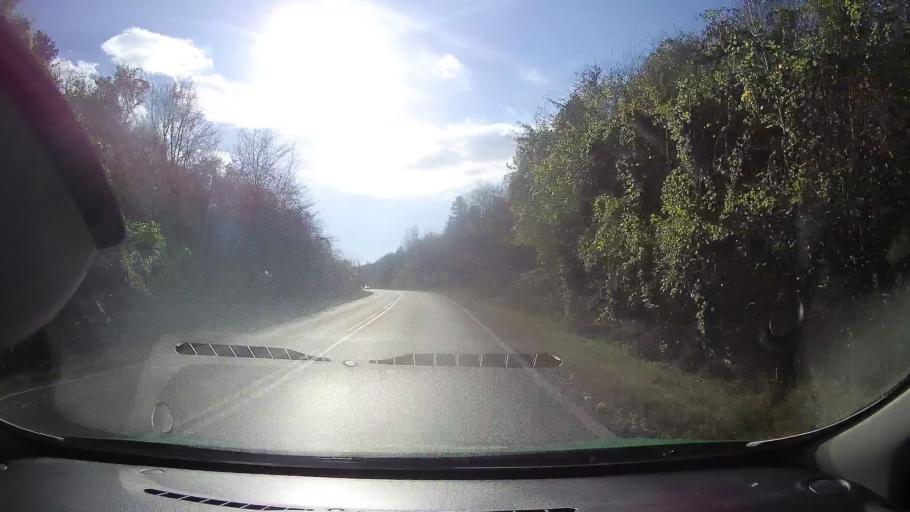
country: RO
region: Tulcea
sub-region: Oras Babadag
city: Babadag
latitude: 44.8707
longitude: 28.6885
